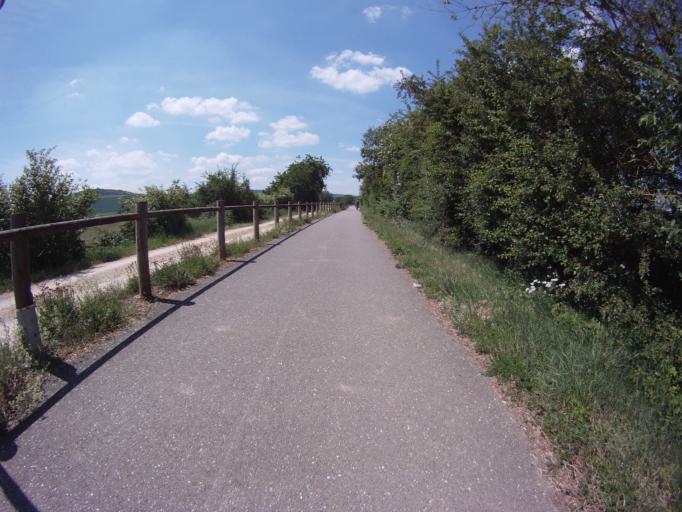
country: FR
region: Lorraine
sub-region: Departement de Meurthe-et-Moselle
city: Seichamps
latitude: 48.7381
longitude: 6.2619
